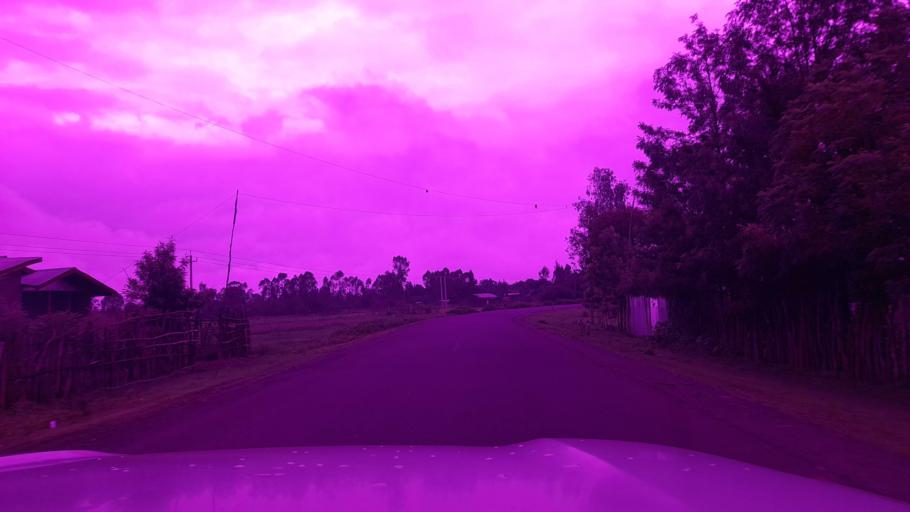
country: ET
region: Oromiya
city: Waliso
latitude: 8.2725
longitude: 37.6618
